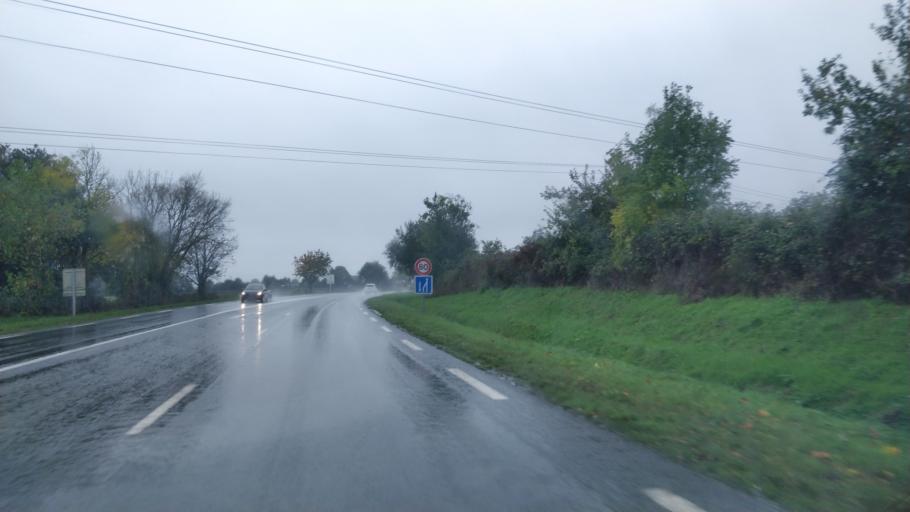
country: FR
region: Lower Normandy
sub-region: Departement de la Manche
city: Saint-Planchers
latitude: 48.8444
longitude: -1.5411
